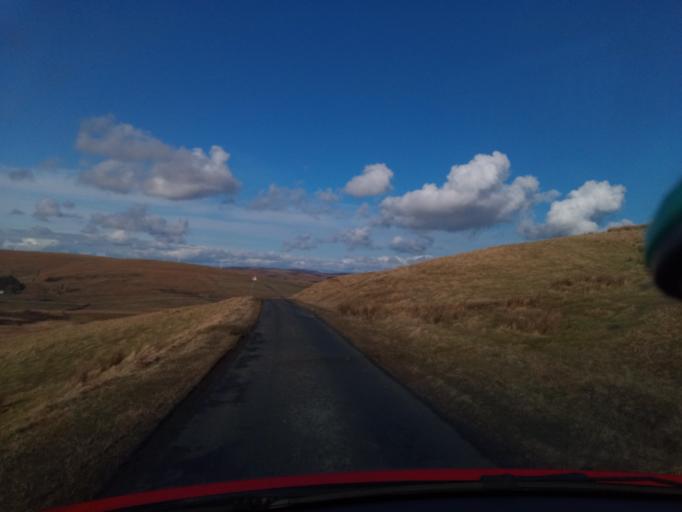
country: GB
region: Scotland
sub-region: The Scottish Borders
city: Hawick
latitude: 55.4458
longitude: -2.8872
